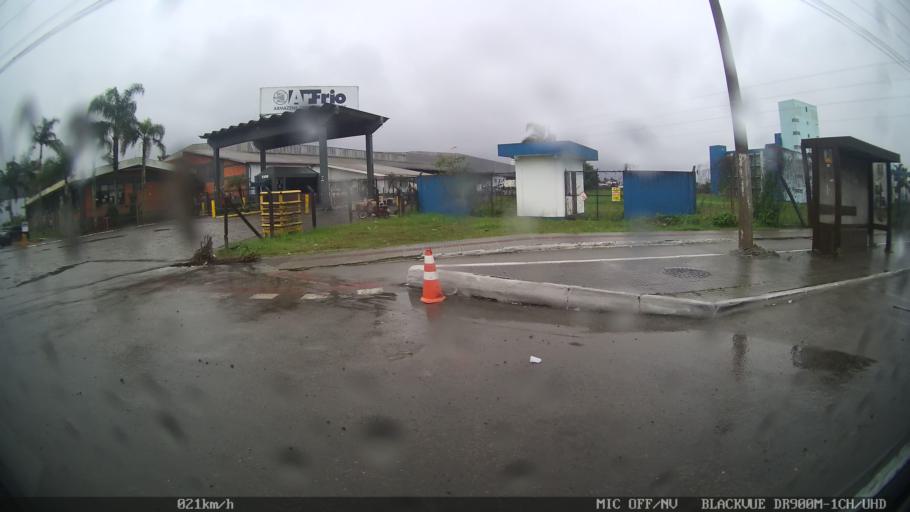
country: BR
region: Santa Catarina
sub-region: Itajai
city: Itajai
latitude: -26.9163
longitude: -48.7029
